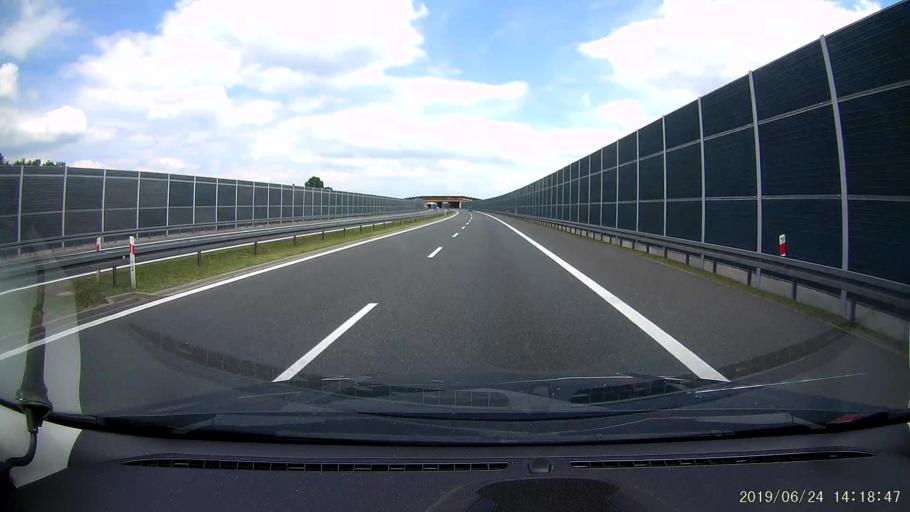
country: PL
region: Lesser Poland Voivodeship
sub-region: Powiat bochenski
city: Stanislawice
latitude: 49.9949
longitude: 20.3792
